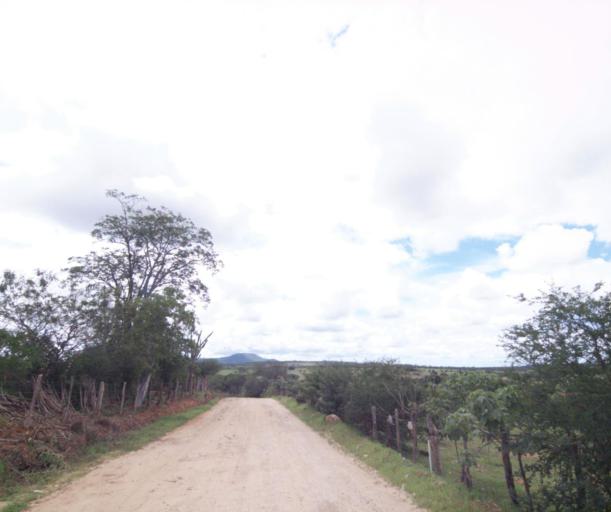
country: BR
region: Bahia
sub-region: Tanhacu
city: Tanhacu
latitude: -14.1630
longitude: -41.1721
